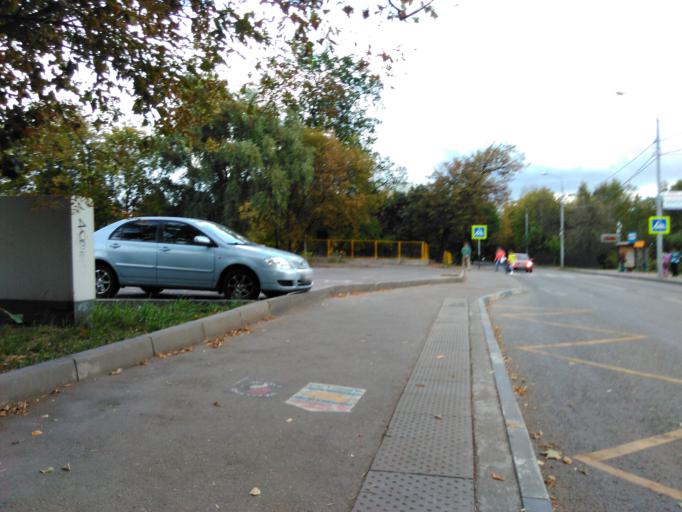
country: RU
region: Moscow
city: Sviblovo
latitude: 55.8449
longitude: 37.6381
